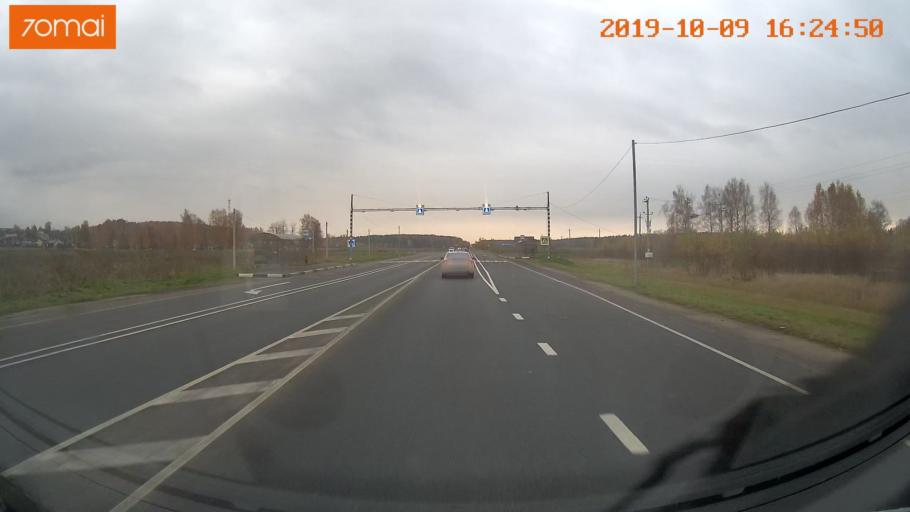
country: RU
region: Kostroma
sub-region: Kostromskoy Rayon
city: Kostroma
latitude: 57.6481
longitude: 40.9144
